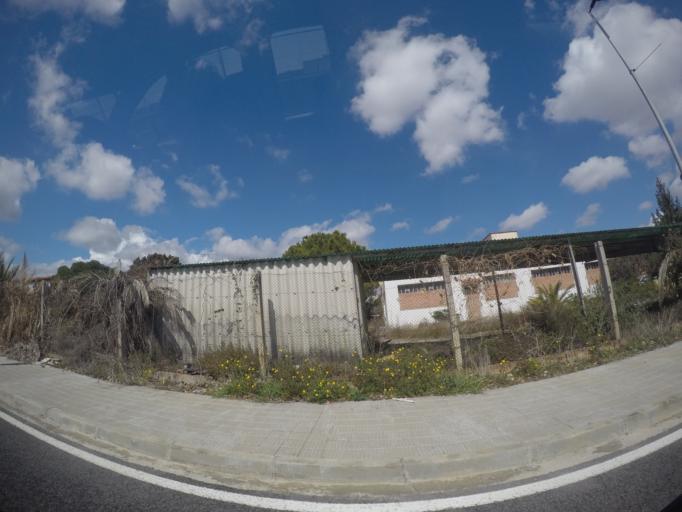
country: ES
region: Catalonia
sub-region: Provincia de Tarragona
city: Sant Jaume dels Domenys
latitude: 41.2816
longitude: 1.5457
